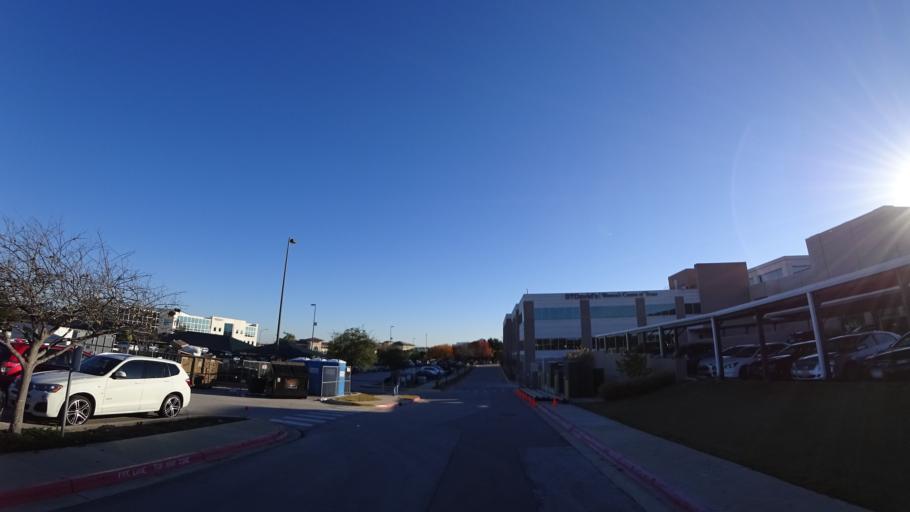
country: US
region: Texas
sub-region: Travis County
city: Wells Branch
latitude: 30.4126
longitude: -97.7050
